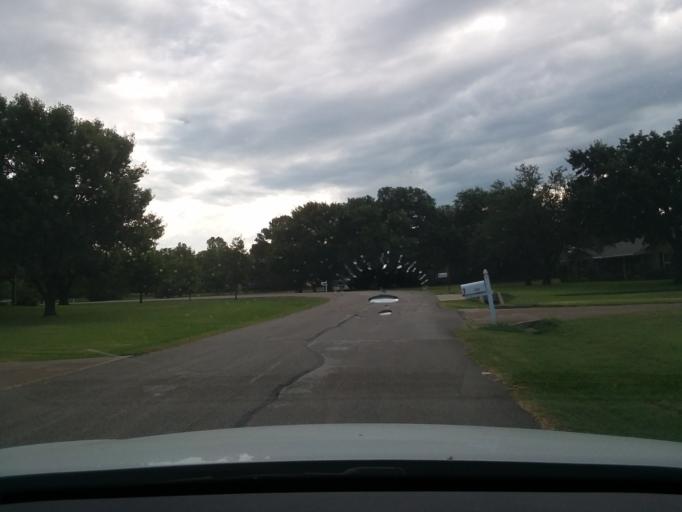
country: US
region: Texas
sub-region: Denton County
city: Double Oak
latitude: 33.0664
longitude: -97.1056
